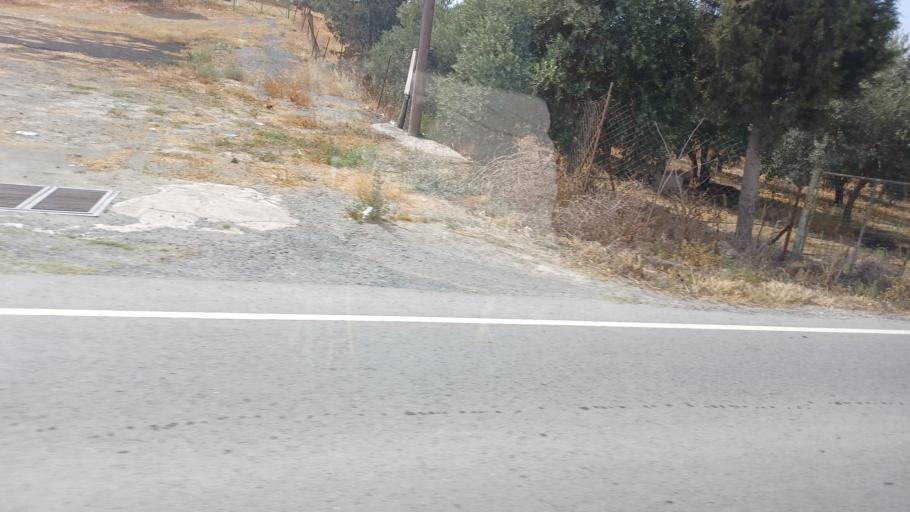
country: CY
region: Larnaka
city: Aradippou
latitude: 34.9407
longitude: 33.5553
